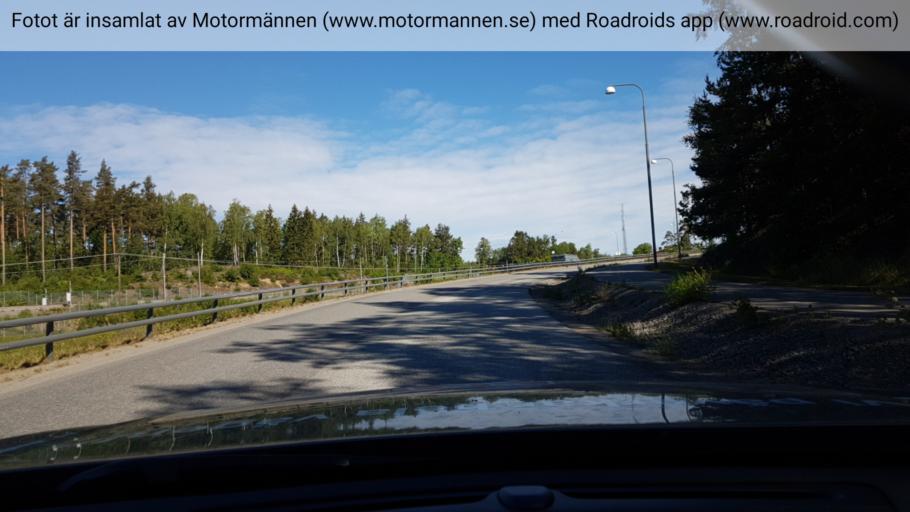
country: SE
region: Stockholm
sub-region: Nynashamns Kommun
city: Osmo
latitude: 58.9794
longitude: 17.9048
